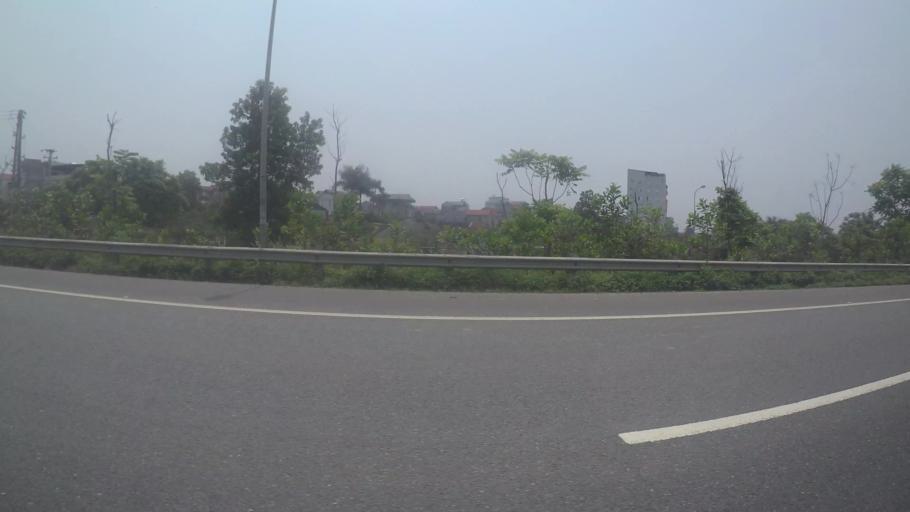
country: VN
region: Ha Noi
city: Troi
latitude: 21.0097
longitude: 105.7106
